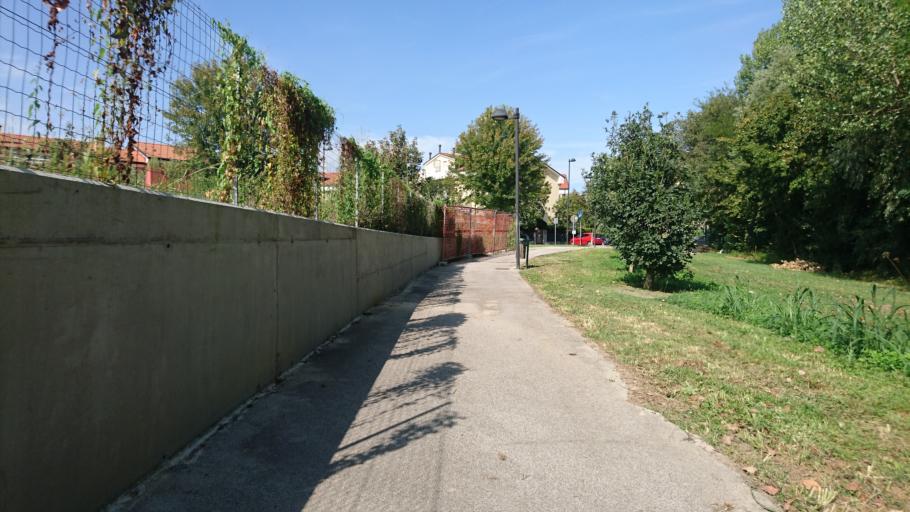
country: IT
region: Veneto
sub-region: Provincia di Padova
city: Veggiano
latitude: 45.4449
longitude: 11.7111
